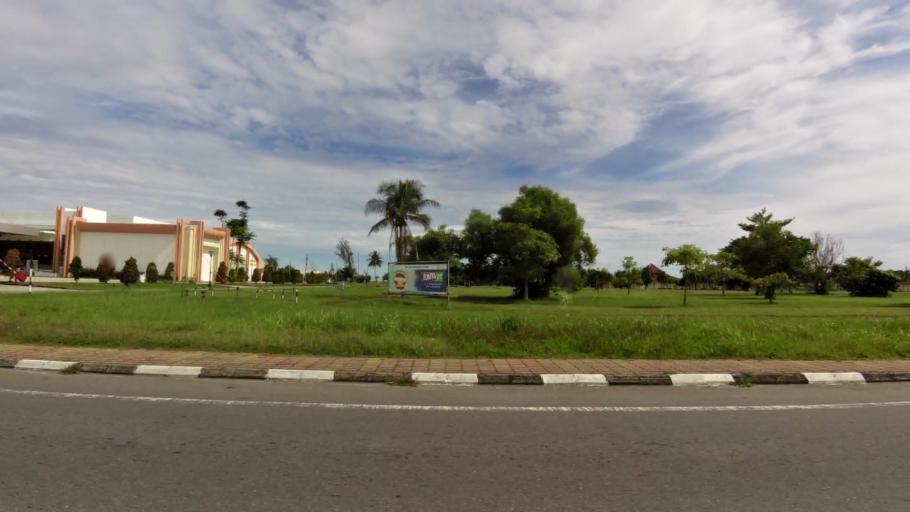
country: BN
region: Belait
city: Seria
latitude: 4.6145
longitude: 114.3263
